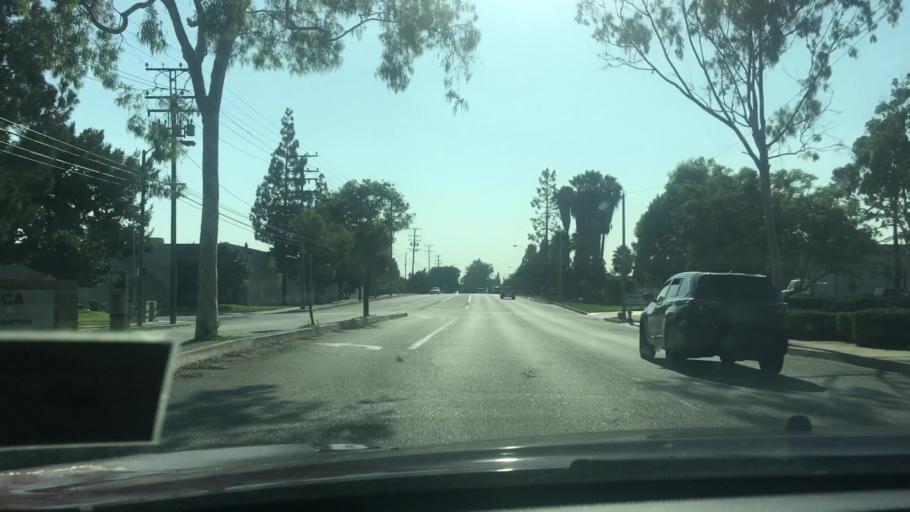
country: US
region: California
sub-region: Orange County
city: La Palma
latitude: 33.8734
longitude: -118.0305
